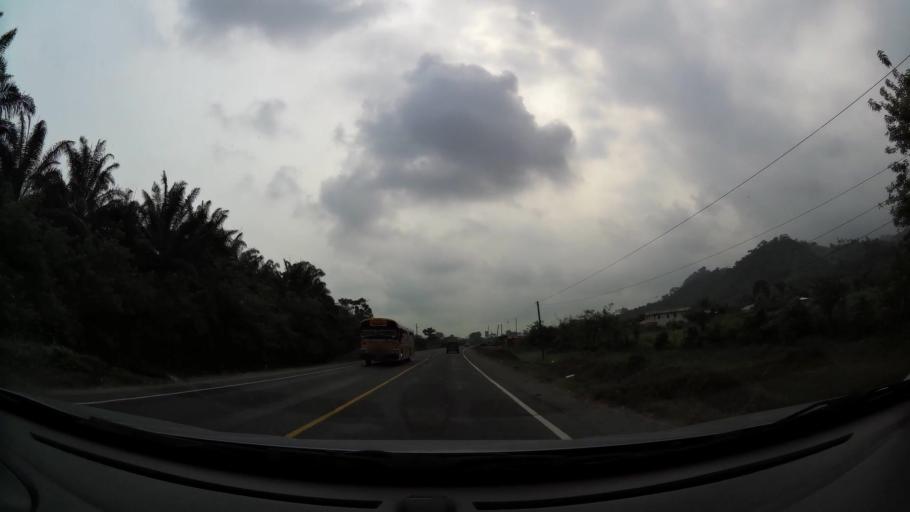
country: HN
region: Yoro
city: Guaimitas
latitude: 15.4919
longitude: -87.7513
